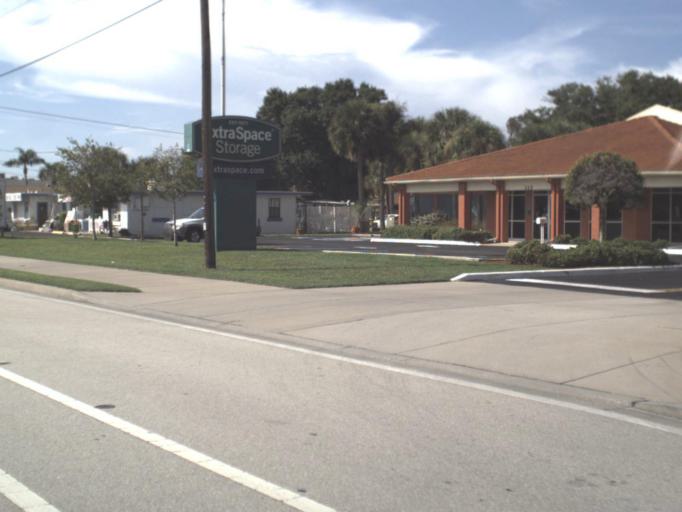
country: US
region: Florida
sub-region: Sarasota County
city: Nokomis
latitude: 27.1272
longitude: -82.4537
